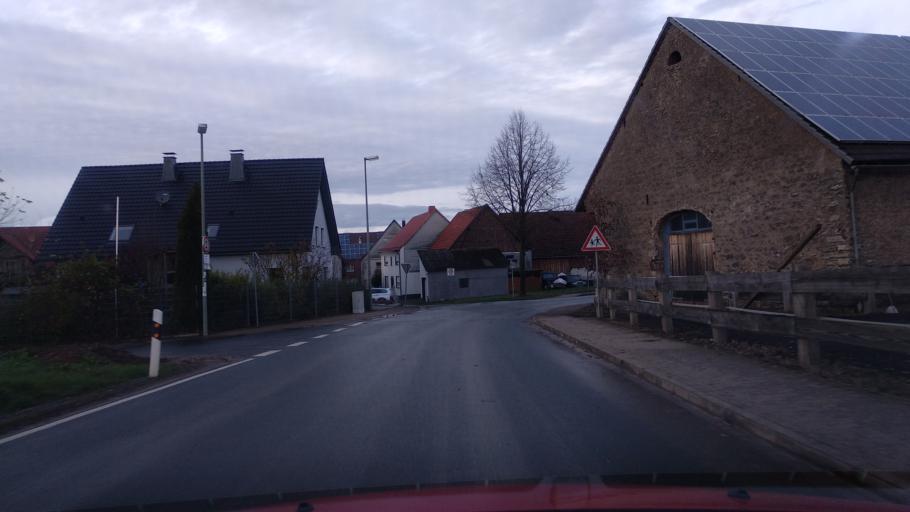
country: DE
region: North Rhine-Westphalia
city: Brakel
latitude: 51.6871
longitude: 9.2246
